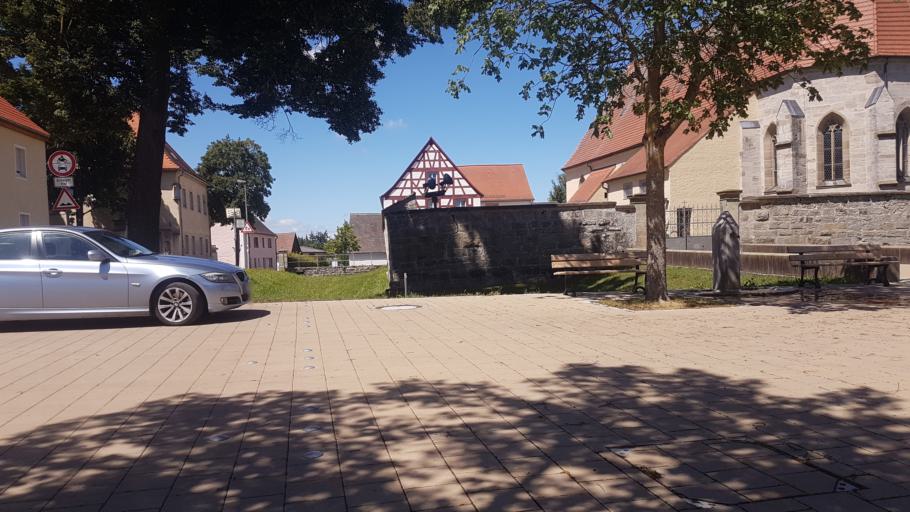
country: DE
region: Bavaria
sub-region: Regierungsbezirk Mittelfranken
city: Aurach
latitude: 49.2611
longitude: 10.4591
